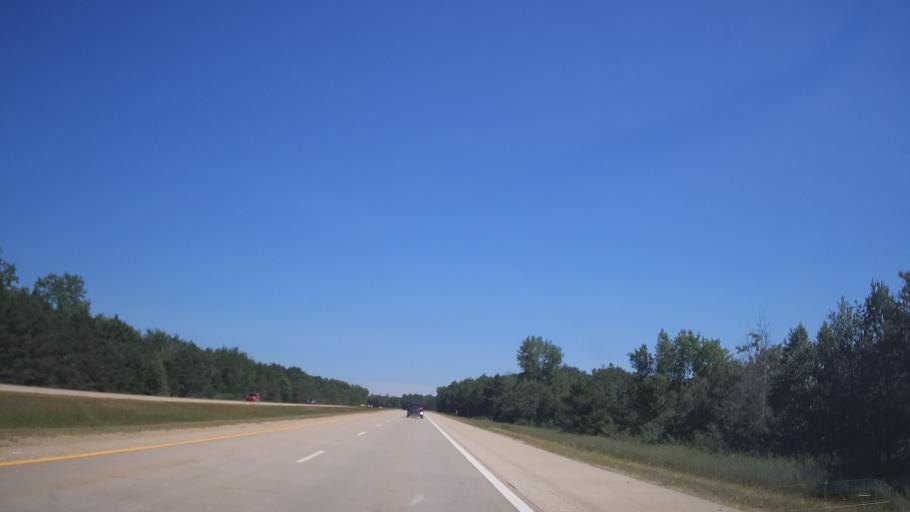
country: US
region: Michigan
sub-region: Midland County
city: Coleman
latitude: 43.7551
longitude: -84.5485
